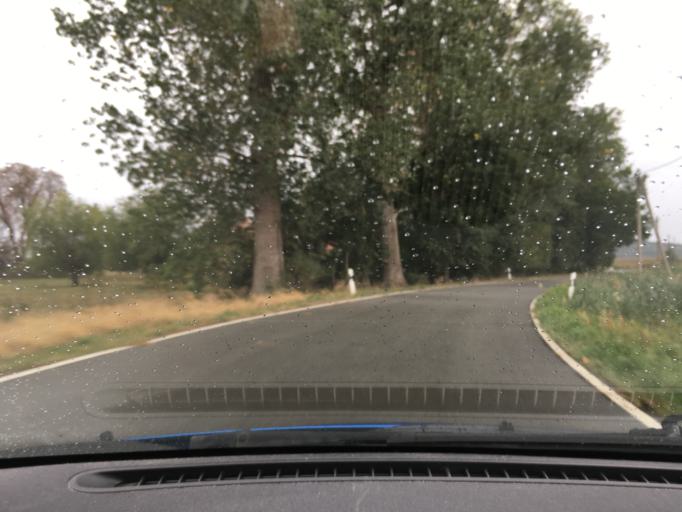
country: DE
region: Lower Saxony
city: Hitzacker
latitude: 53.1917
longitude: 11.0051
